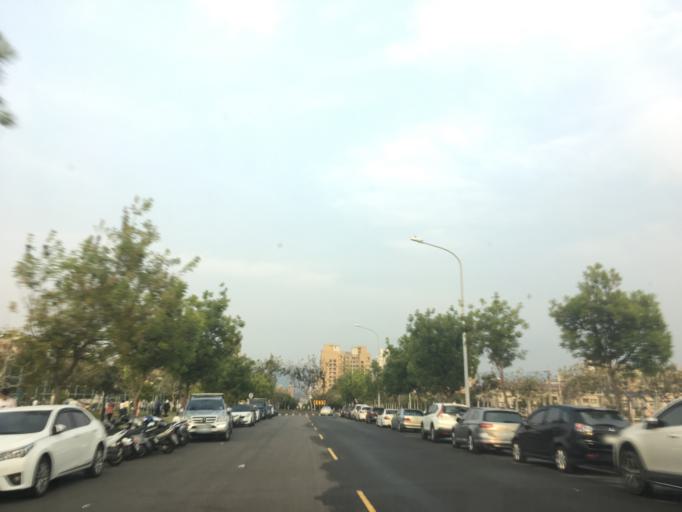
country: TW
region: Taiwan
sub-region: Taichung City
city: Taichung
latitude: 24.1783
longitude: 120.7081
